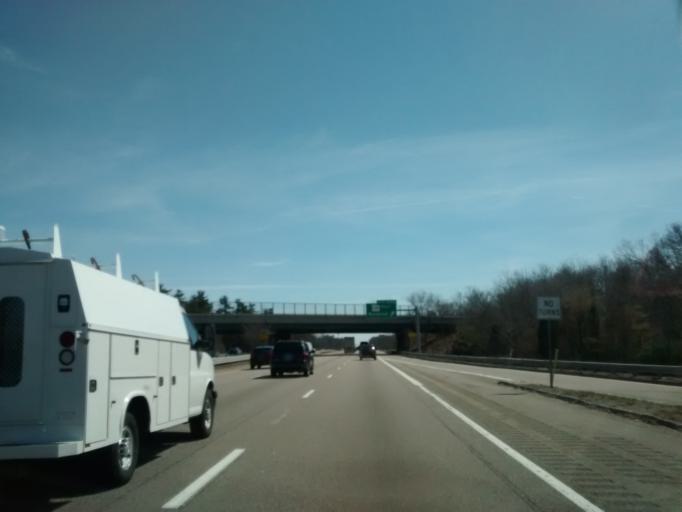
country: US
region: Massachusetts
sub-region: Norfolk County
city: Randolph
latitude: 42.1582
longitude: -71.0694
